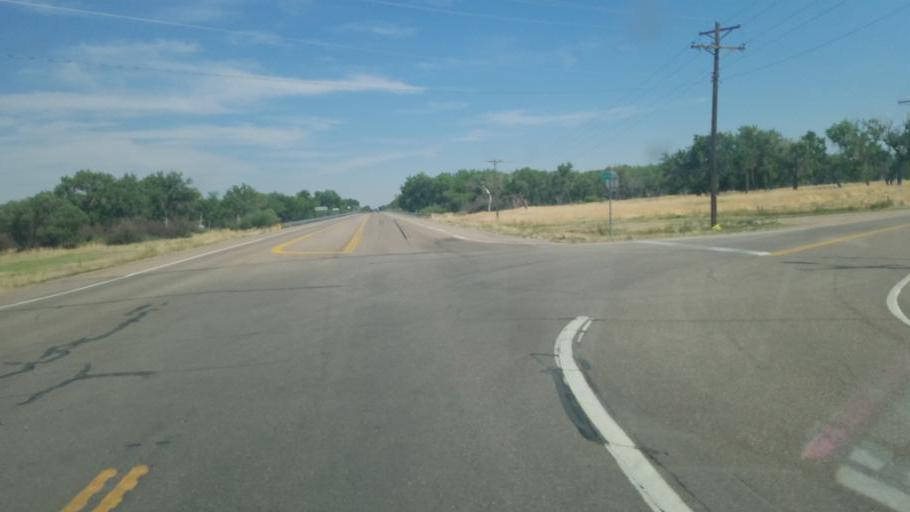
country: US
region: Colorado
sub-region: Pueblo County
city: Pueblo
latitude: 38.2480
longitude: -104.3491
